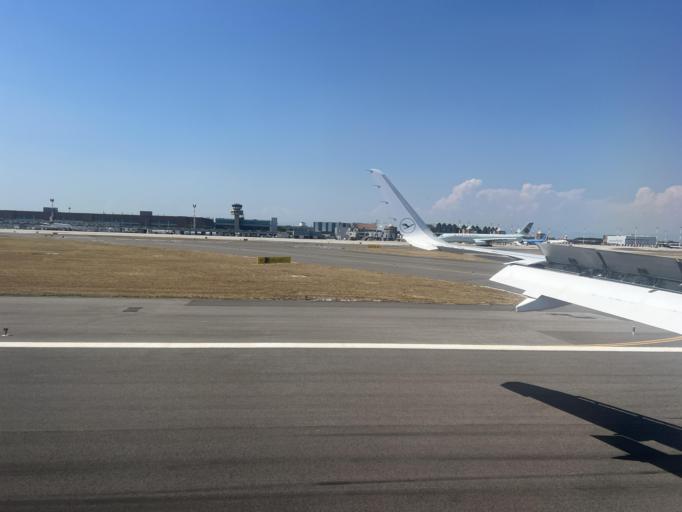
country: IT
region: Veneto
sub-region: Provincia di Venezia
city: Tessera
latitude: 45.5003
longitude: 12.3448
